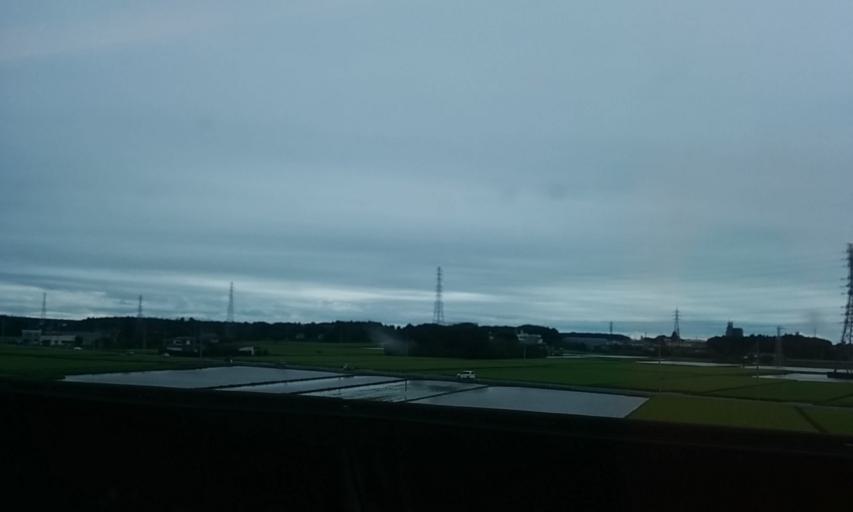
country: JP
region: Tochigi
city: Utsunomiya-shi
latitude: 36.5955
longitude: 139.9052
